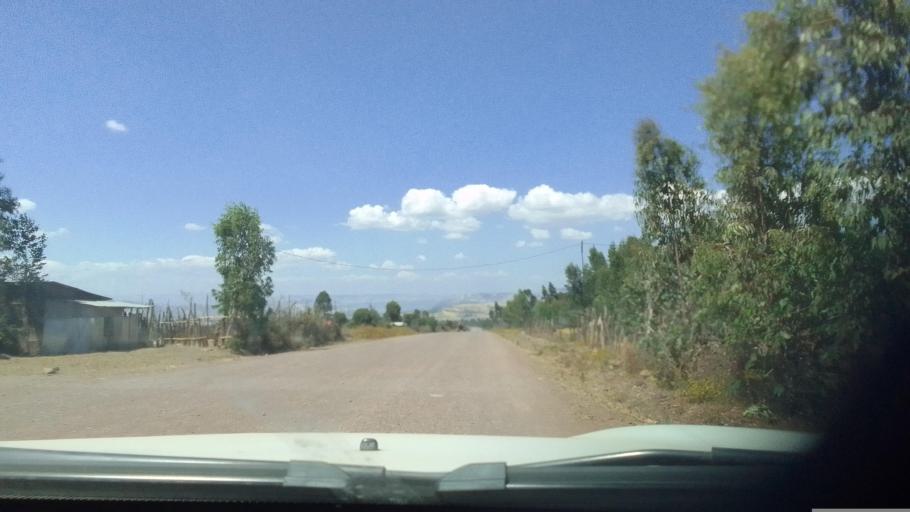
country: ET
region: Oromiya
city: Hagere Hiywet
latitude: 8.9231
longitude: 37.8642
